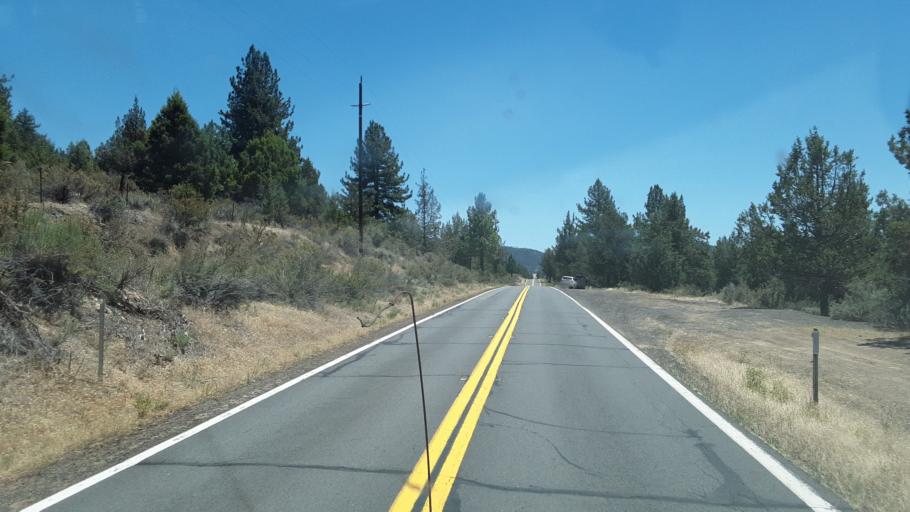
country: US
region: California
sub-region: Modoc County
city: Alturas
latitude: 41.0697
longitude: -120.8851
